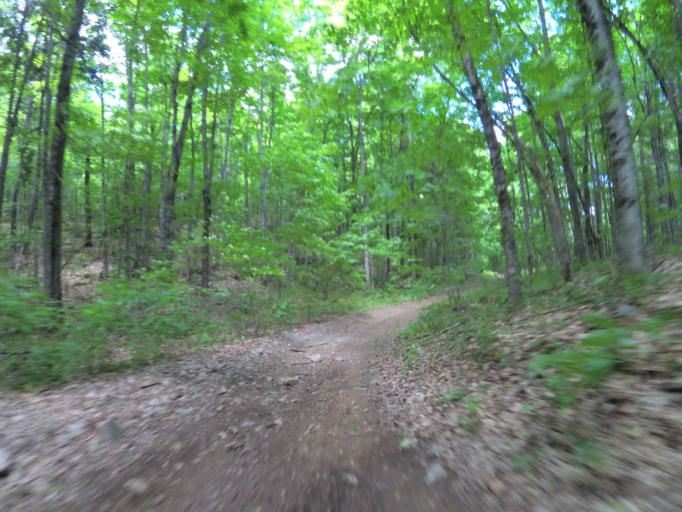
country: CA
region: Ontario
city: Renfrew
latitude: 45.0553
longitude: -76.8604
